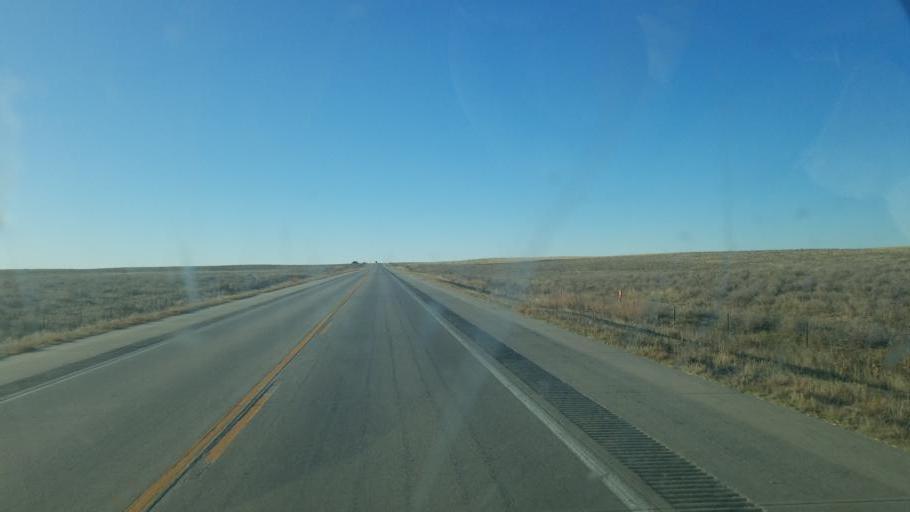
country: US
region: Colorado
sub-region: Kiowa County
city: Eads
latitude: 38.6038
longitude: -102.7858
